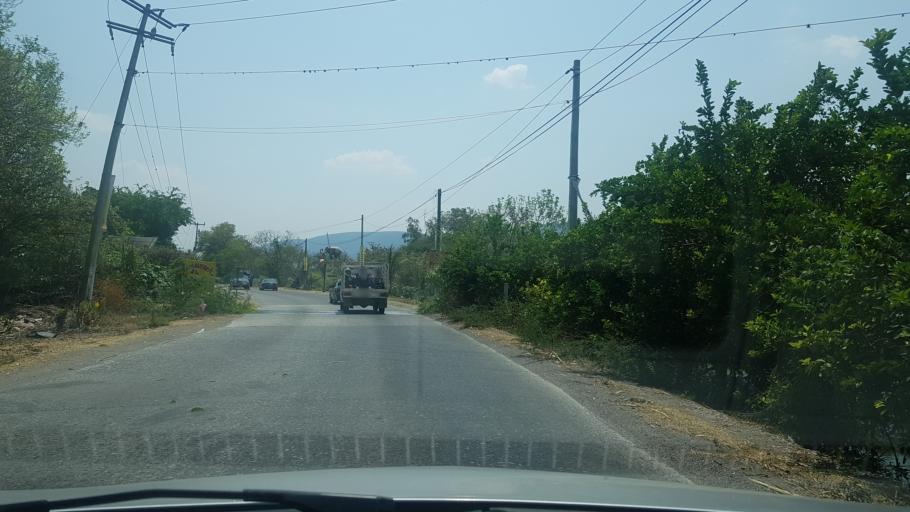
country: MX
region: Morelos
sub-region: Jiutepec
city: Independencia
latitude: 18.7997
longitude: -99.1009
